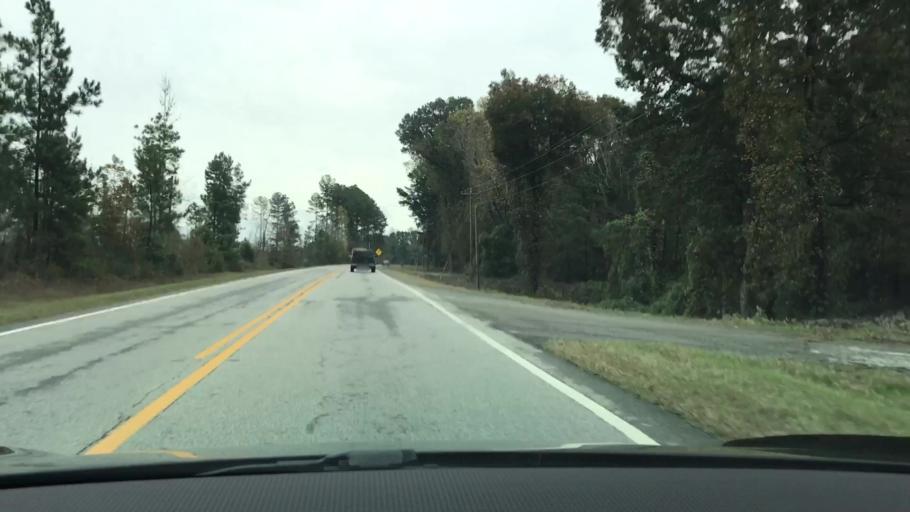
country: US
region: Georgia
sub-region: Greene County
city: Greensboro
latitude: 33.6076
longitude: -83.2016
